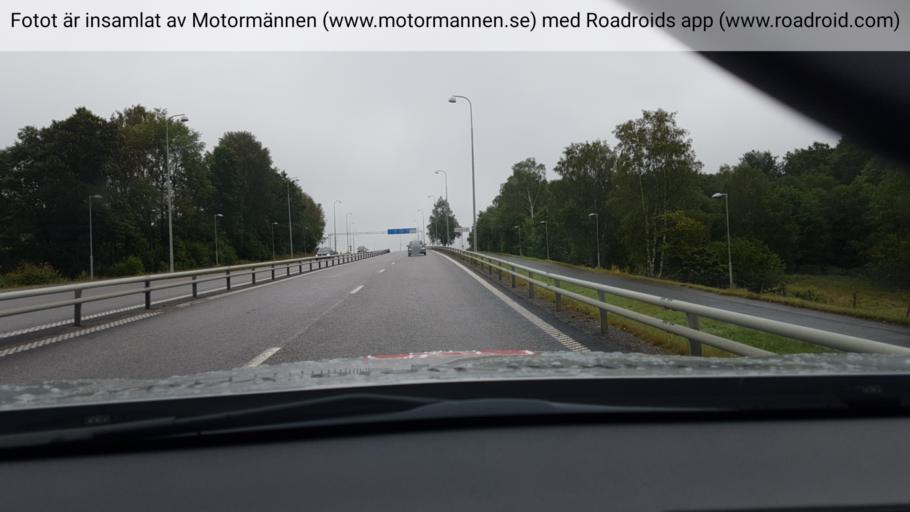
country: SE
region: Vaestra Goetaland
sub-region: Goteborg
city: Rannebergen
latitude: 57.7812
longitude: 12.0780
